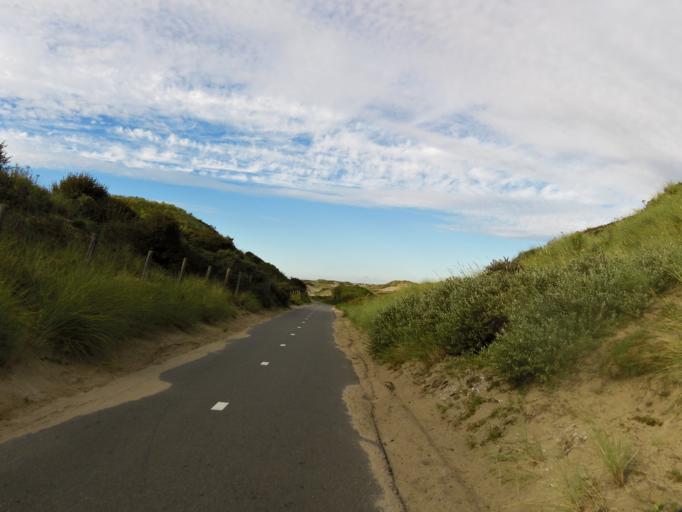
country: NL
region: South Holland
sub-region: Gemeente Katwijk
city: Katwijk aan Zee
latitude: 52.2208
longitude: 4.4102
